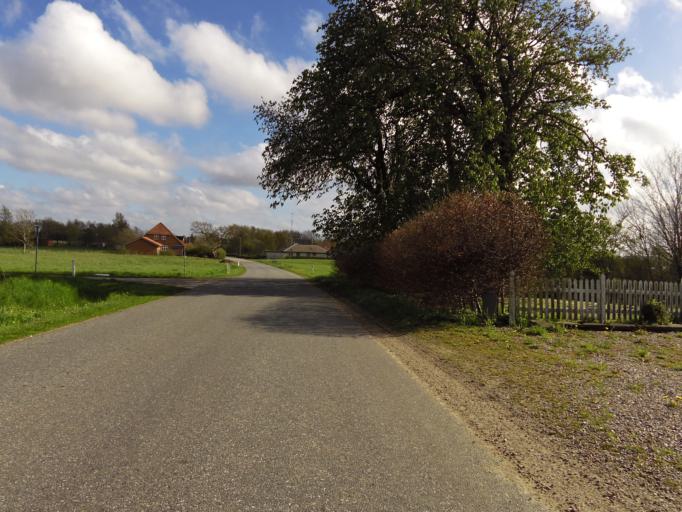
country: DK
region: South Denmark
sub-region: Haderslev Kommune
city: Gram
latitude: 55.3192
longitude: 8.9816
